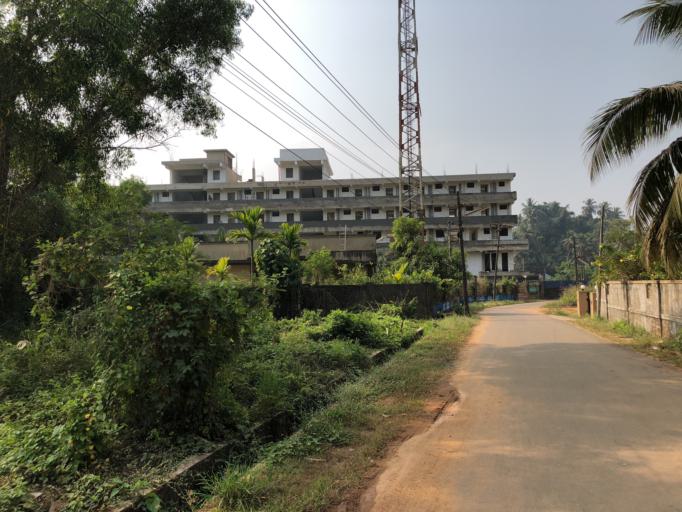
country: IN
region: Karnataka
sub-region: Dakshina Kannada
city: Mangalore
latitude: 12.8719
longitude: 74.8957
